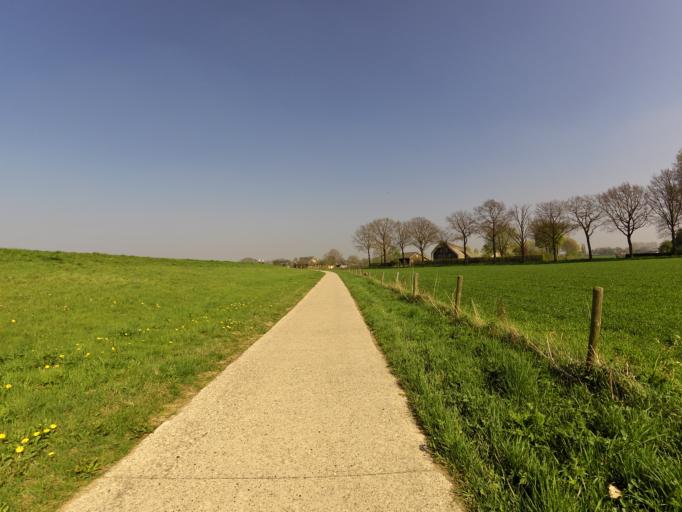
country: NL
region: Gelderland
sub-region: Gemeente Doesburg
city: Doesburg
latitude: 52.0220
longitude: 6.1532
